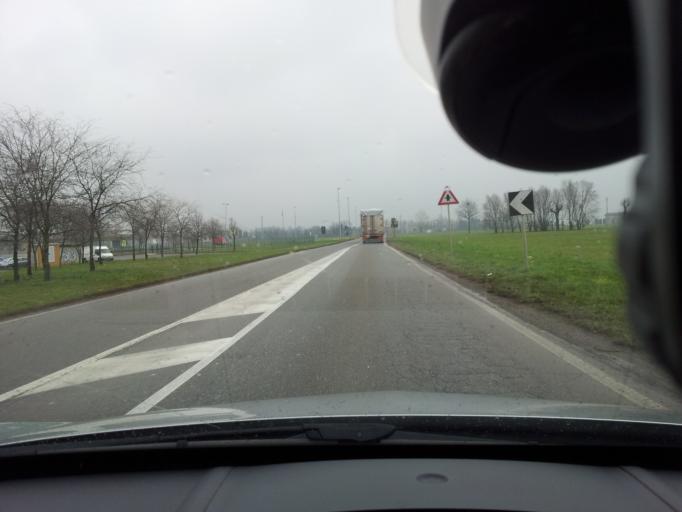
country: IT
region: Lombardy
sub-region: Provincia di Bergamo
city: Cavernago
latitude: 45.6170
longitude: 9.7797
